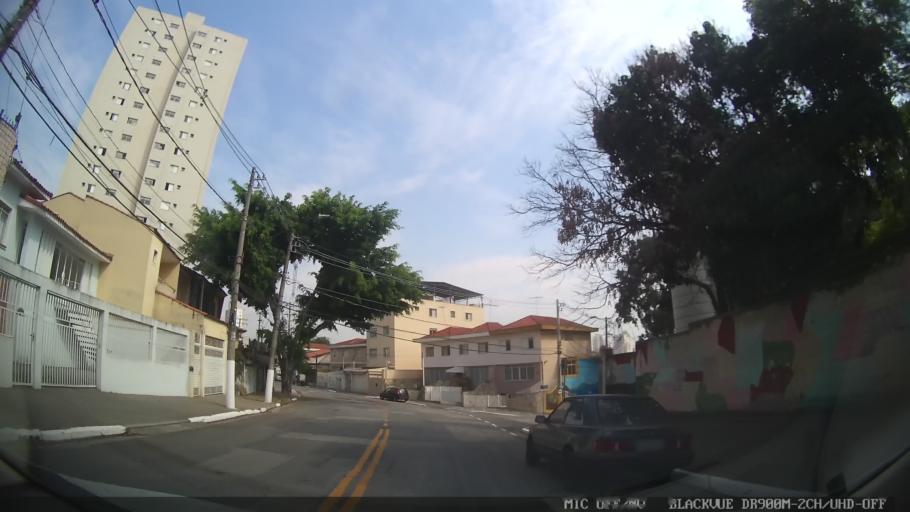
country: BR
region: Sao Paulo
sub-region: Sao Caetano Do Sul
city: Sao Caetano do Sul
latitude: -23.6065
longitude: -46.6023
